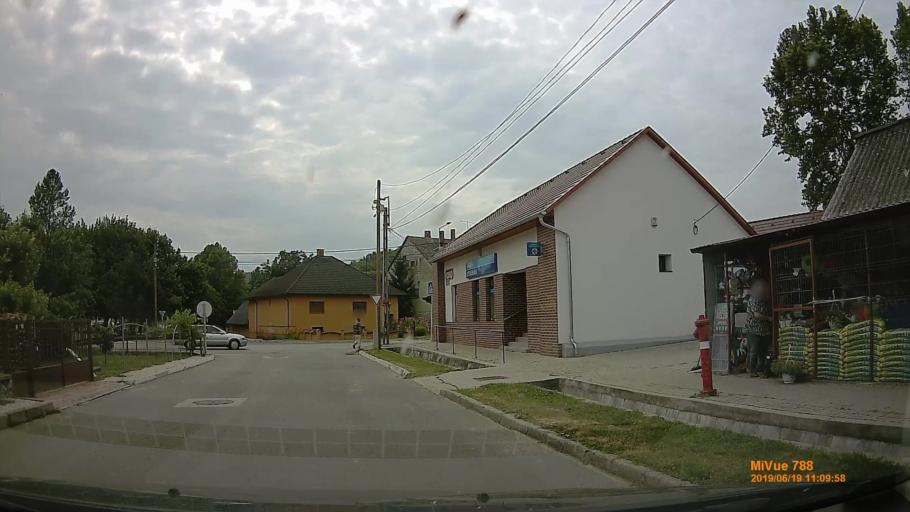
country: HU
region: Tolna
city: Szentgalpuszta
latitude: 46.3464
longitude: 18.5927
